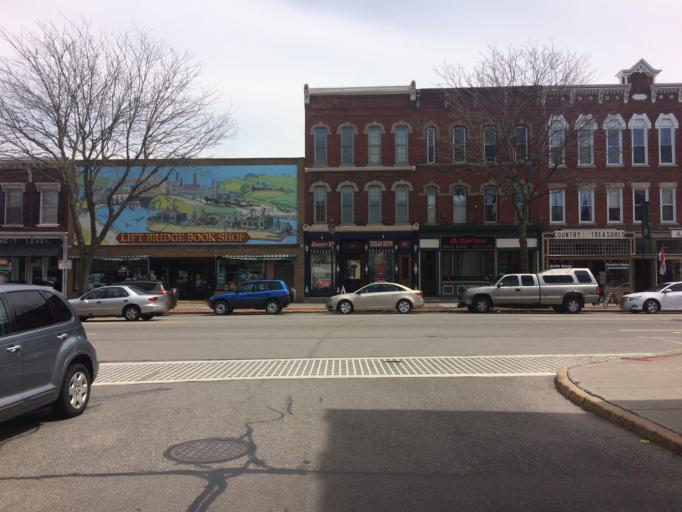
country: US
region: New York
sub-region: Monroe County
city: Brockport
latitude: 43.2153
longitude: -77.9389
